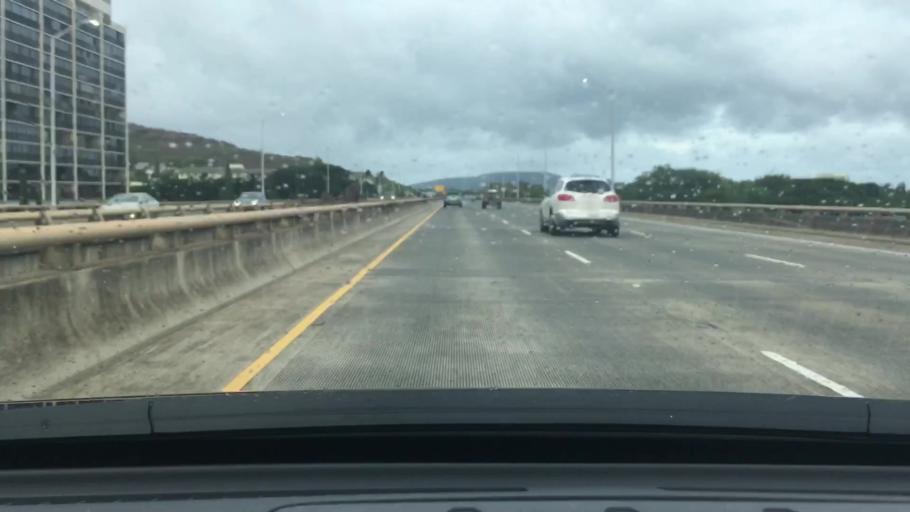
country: US
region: Hawaii
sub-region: Honolulu County
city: Honolulu
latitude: 21.2786
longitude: -157.7867
